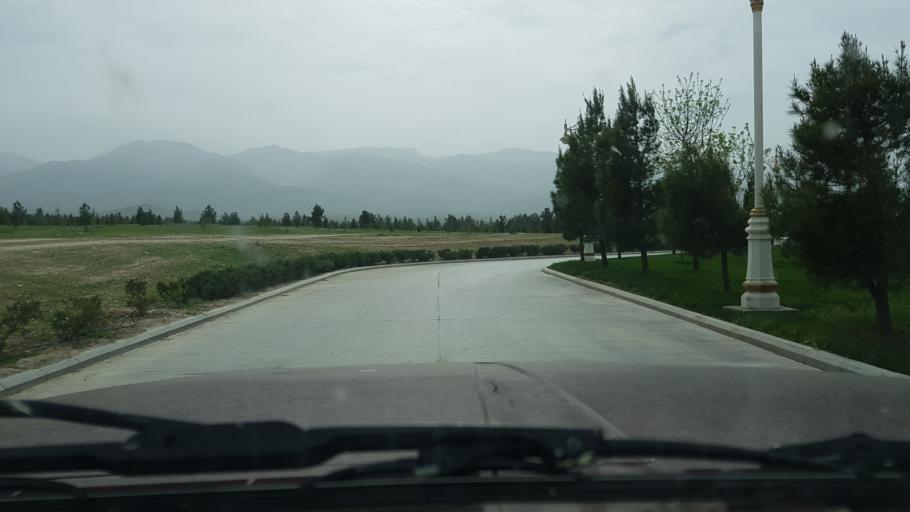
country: TM
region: Ahal
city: Ashgabat
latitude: 37.8813
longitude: 58.3365
